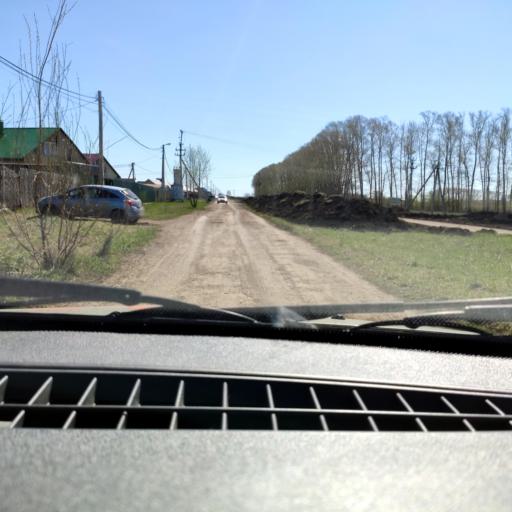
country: RU
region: Bashkortostan
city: Iglino
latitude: 54.8184
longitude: 56.4275
